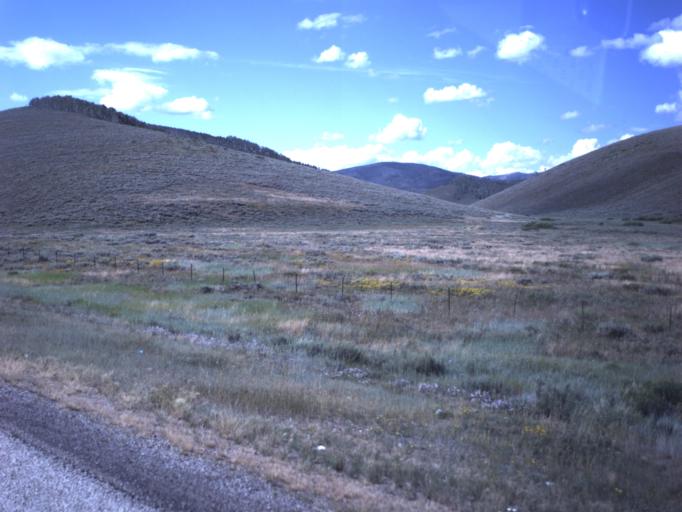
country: US
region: Utah
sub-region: Wasatch County
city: Heber
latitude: 40.2444
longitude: -111.1868
